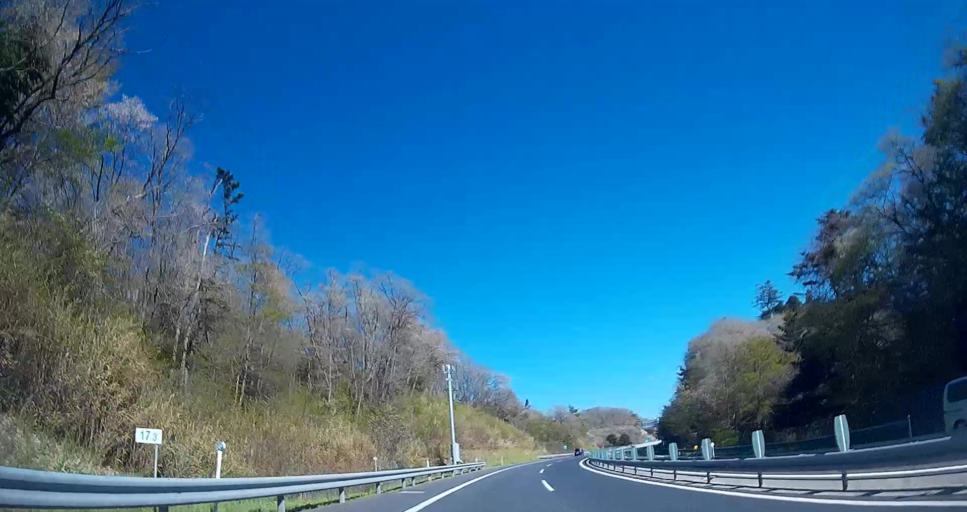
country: JP
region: Miyagi
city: Matsushima
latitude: 38.4044
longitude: 141.0533
